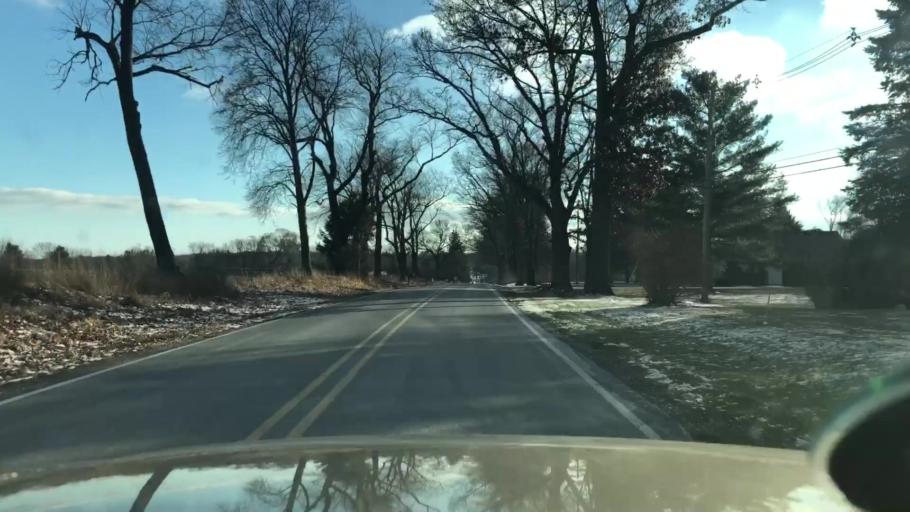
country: US
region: Michigan
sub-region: Jackson County
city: Vandercook Lake
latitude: 42.1673
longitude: -84.4521
